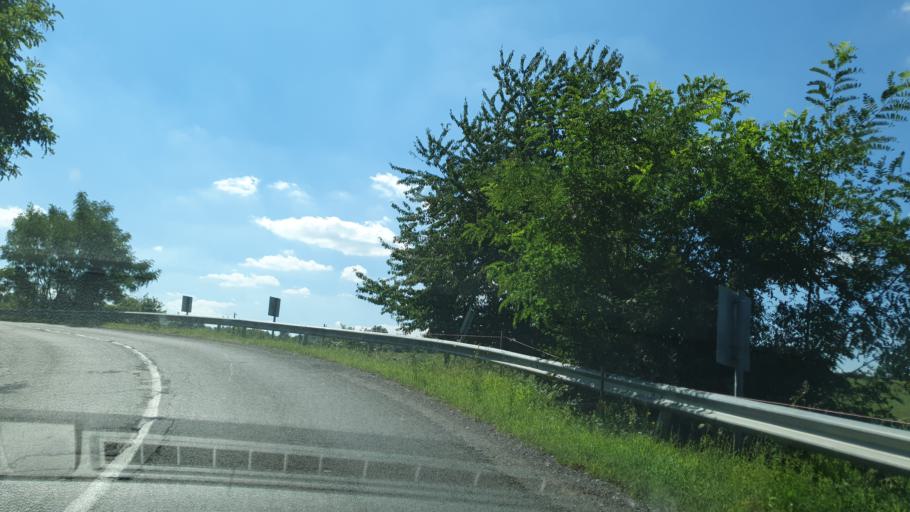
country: HU
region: Nograd
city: Rimoc
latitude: 48.0205
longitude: 19.5954
